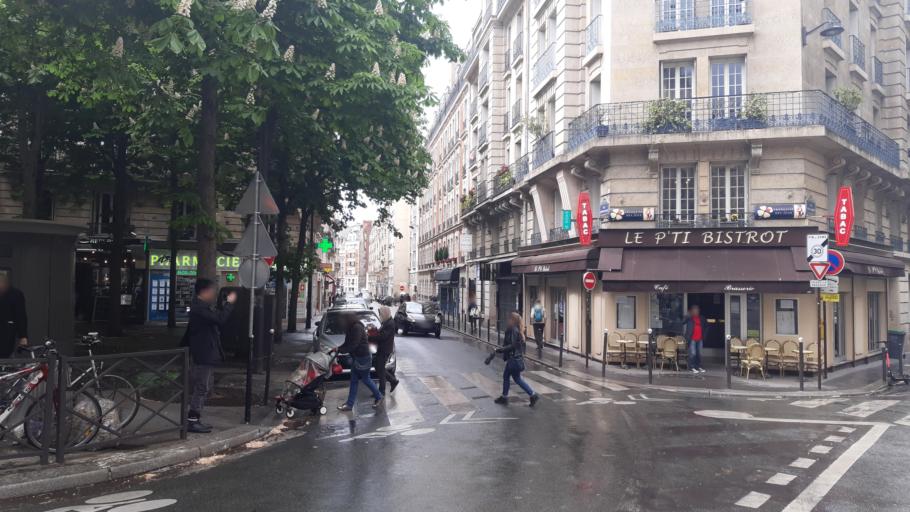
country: FR
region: Ile-de-France
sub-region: Departement des Hauts-de-Seine
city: Vanves
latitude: 48.8362
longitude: 2.2936
